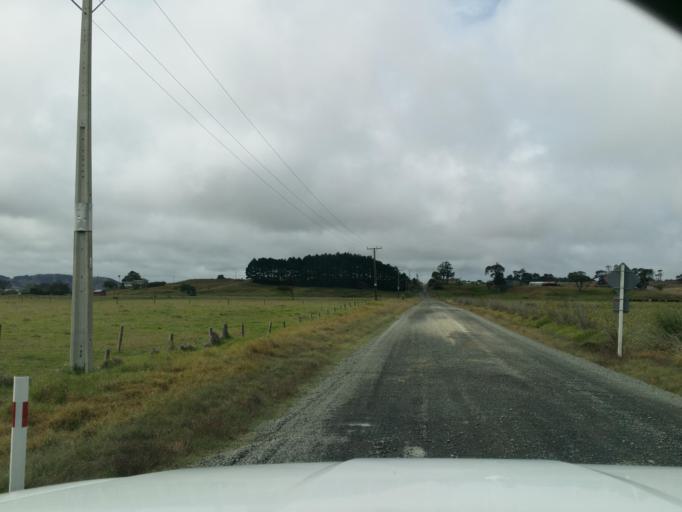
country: NZ
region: Northland
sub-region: Kaipara District
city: Dargaville
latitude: -36.0084
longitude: 173.8878
